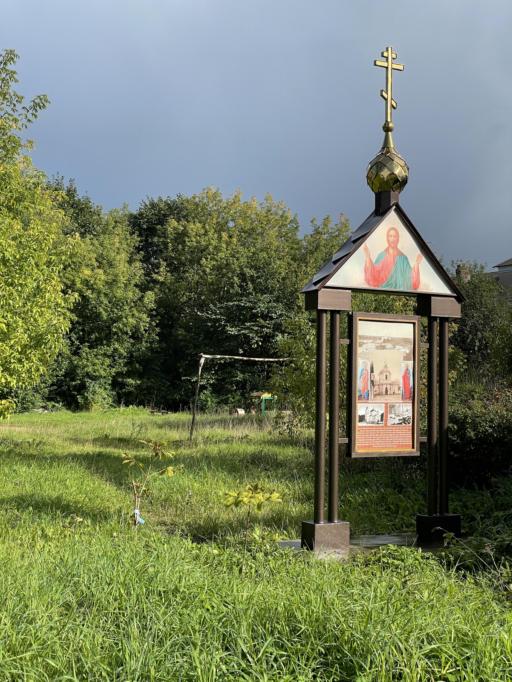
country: RU
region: Tverskaya
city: Vyshniy Volochek
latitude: 57.5849
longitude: 34.5500
